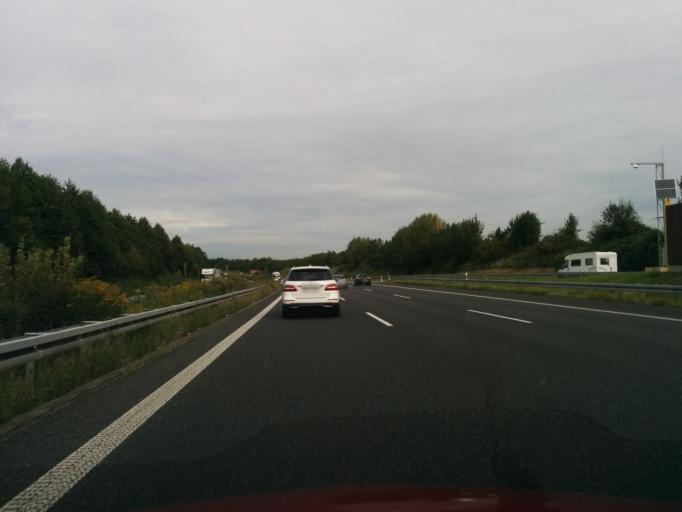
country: DE
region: Baden-Wuerttemberg
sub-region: Karlsruhe Region
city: Ettlingen
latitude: 48.9568
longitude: 8.4811
